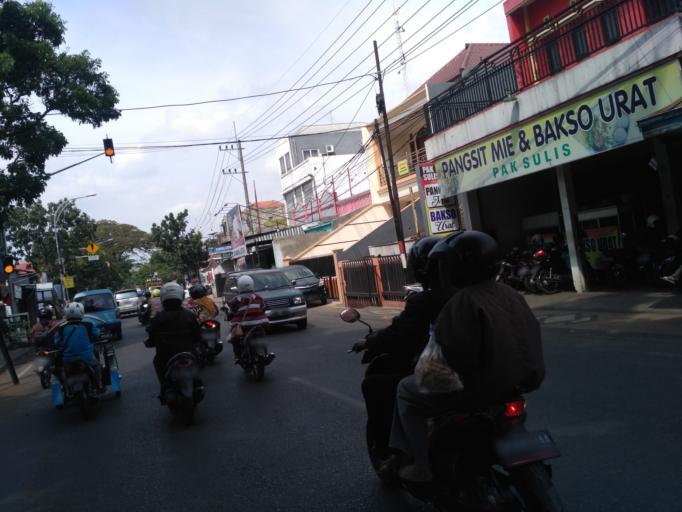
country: ID
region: East Java
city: Malang
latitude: -7.9417
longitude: 112.6445
